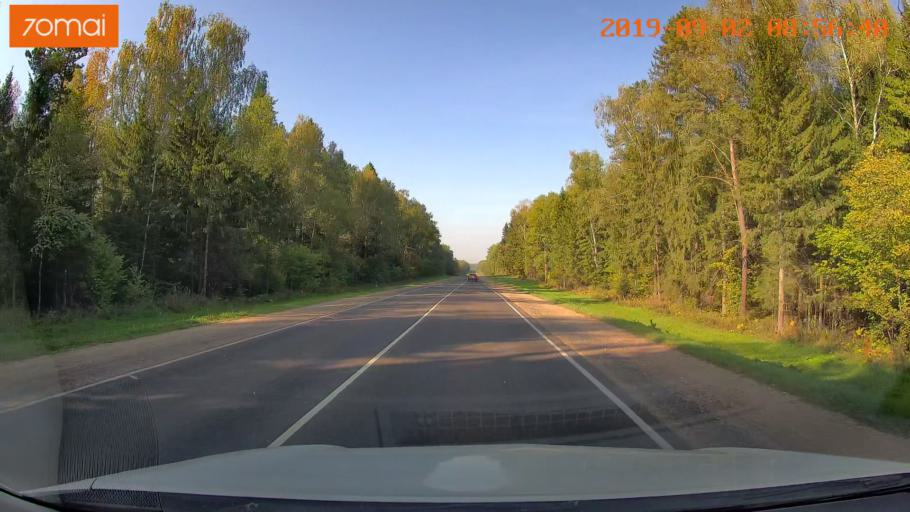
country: RU
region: Kaluga
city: Medyn'
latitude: 54.9435
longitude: 35.7871
